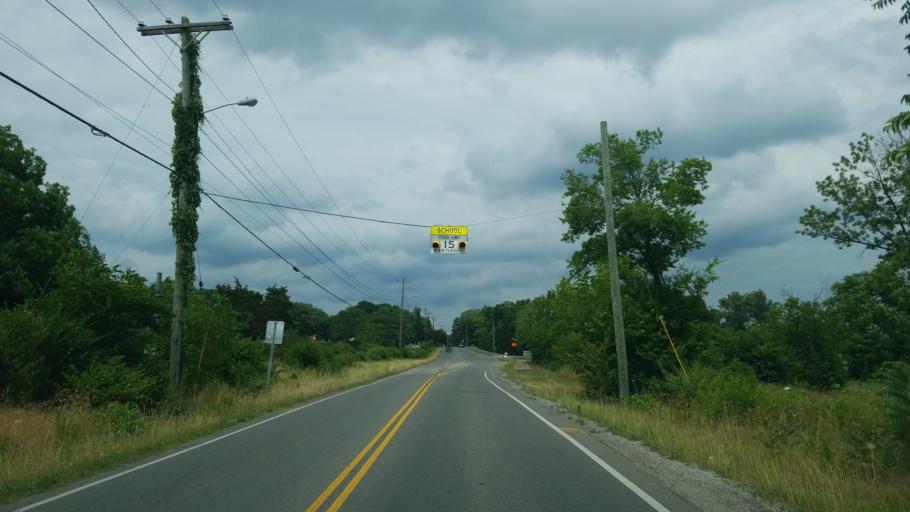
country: US
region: Tennessee
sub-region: Rutherford County
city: La Vergne
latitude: 36.0631
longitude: -86.6074
